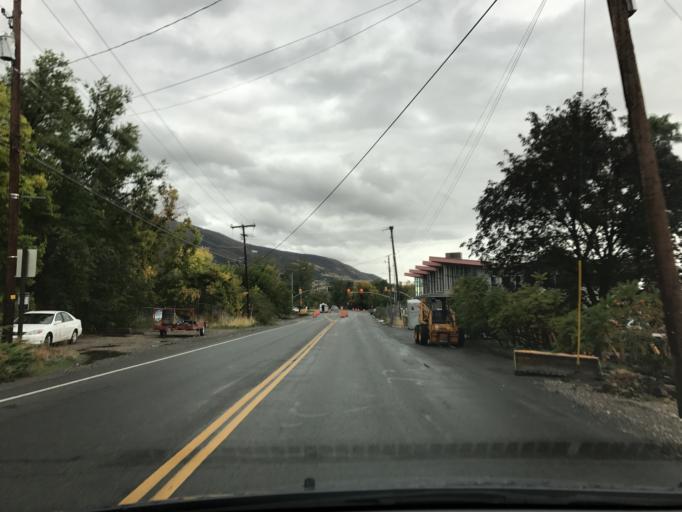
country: US
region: Utah
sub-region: Davis County
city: Farmington
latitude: 40.9927
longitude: -111.8945
